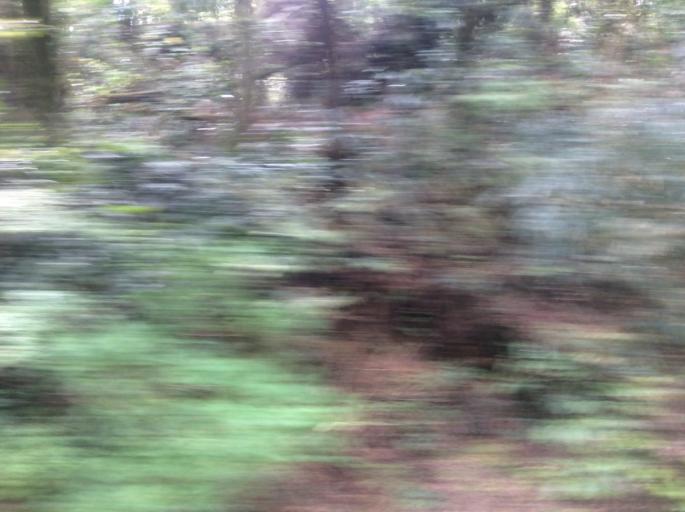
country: TW
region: Taipei
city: Taipei
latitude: 25.1728
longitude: 121.5405
